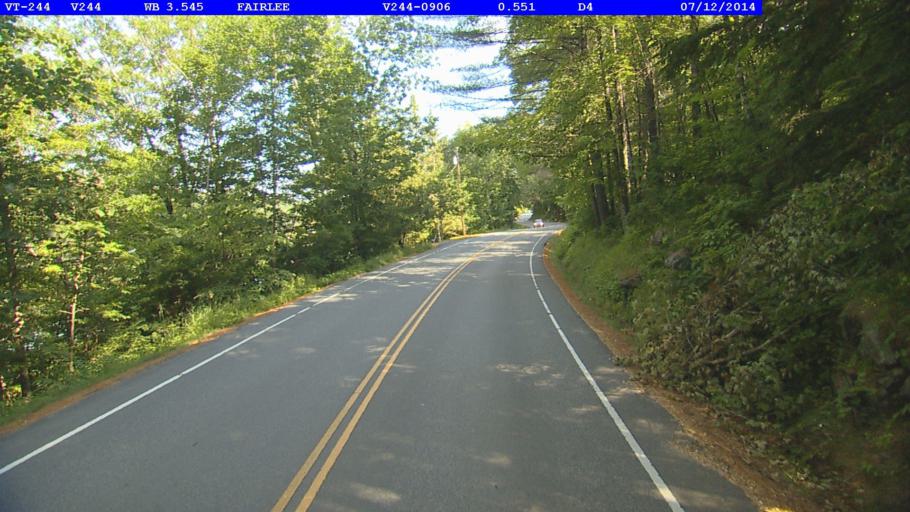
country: US
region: New Hampshire
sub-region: Grafton County
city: Orford
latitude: 43.8968
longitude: -72.2085
